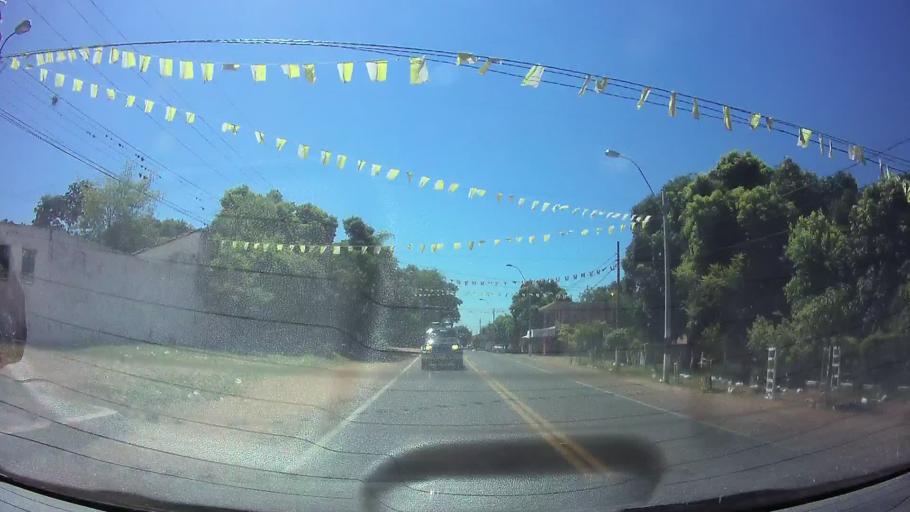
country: PY
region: Central
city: Aregua
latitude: -25.3010
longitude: -57.4069
